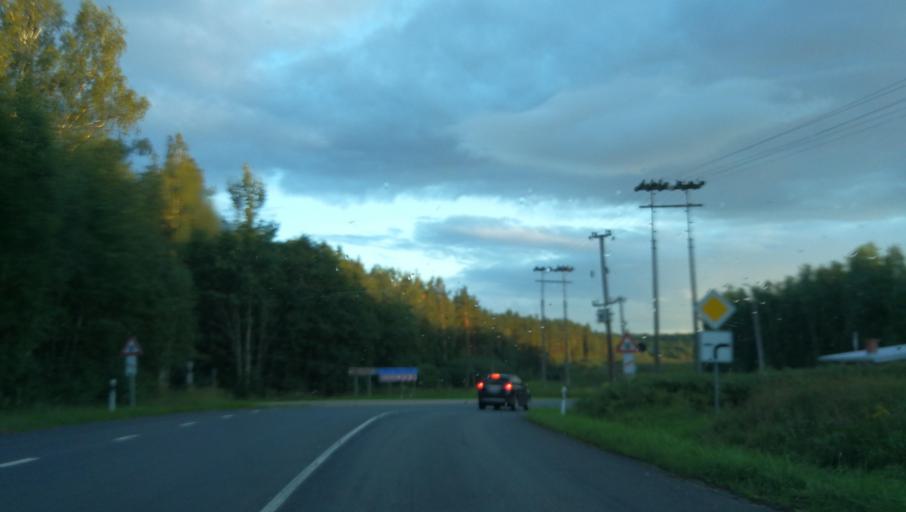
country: LV
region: Priekuli
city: Priekuli
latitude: 57.3655
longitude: 25.3810
